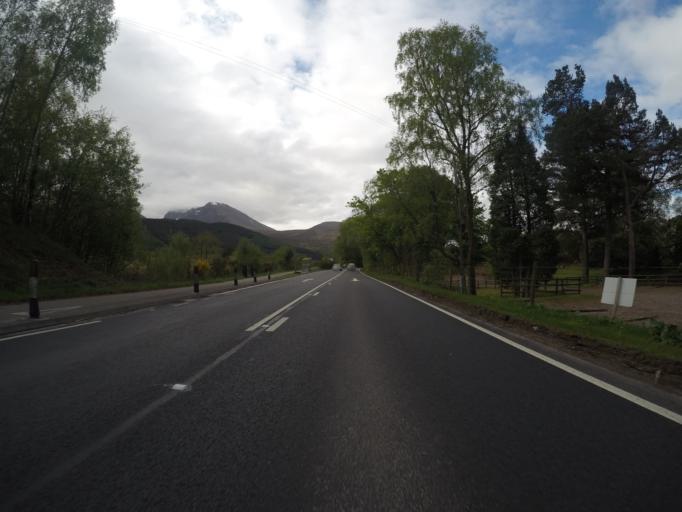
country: GB
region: Scotland
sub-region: Highland
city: Fort William
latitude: 56.8467
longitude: -5.0467
